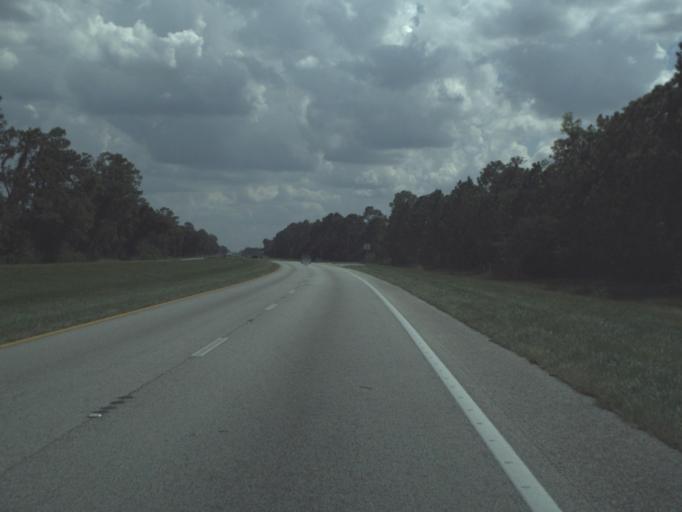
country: US
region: Florida
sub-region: Polk County
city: Crooked Lake Park
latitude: 27.7667
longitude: -81.5957
